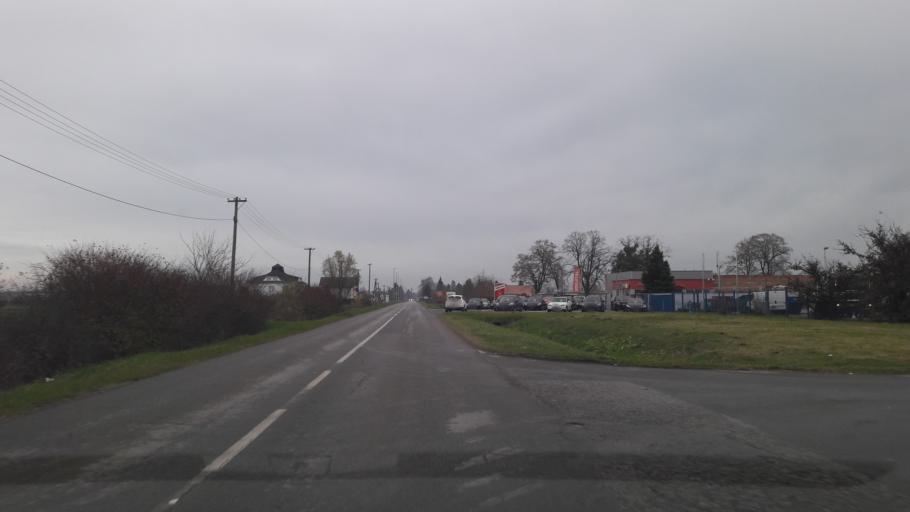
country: HR
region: Osjecko-Baranjska
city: Josipovac
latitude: 45.5920
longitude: 18.5701
